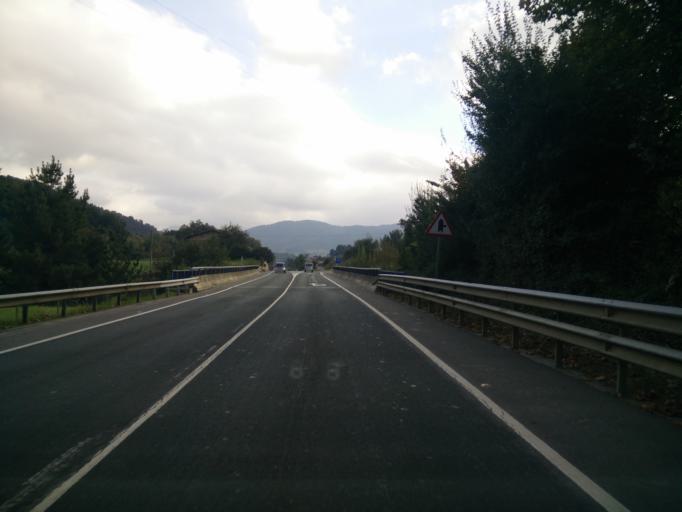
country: ES
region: Basque Country
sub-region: Bizkaia
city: Markina-Xemein
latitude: 43.2836
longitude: -2.4956
